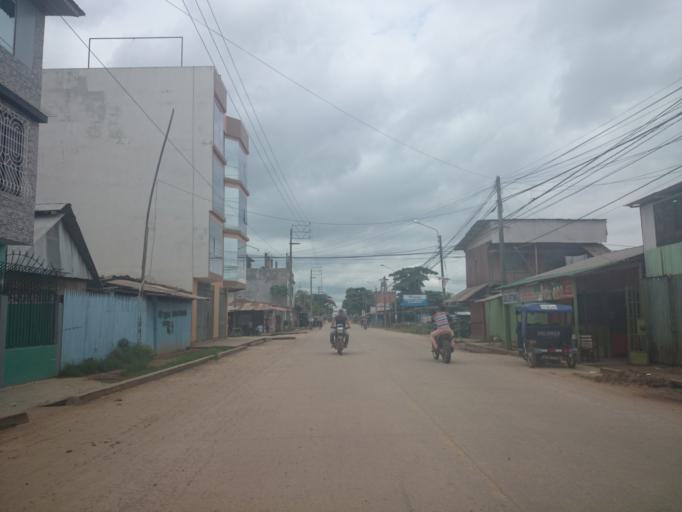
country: PE
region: Ucayali
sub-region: Provincia de Coronel Portillo
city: Pucallpa
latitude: -8.3759
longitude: -74.5583
